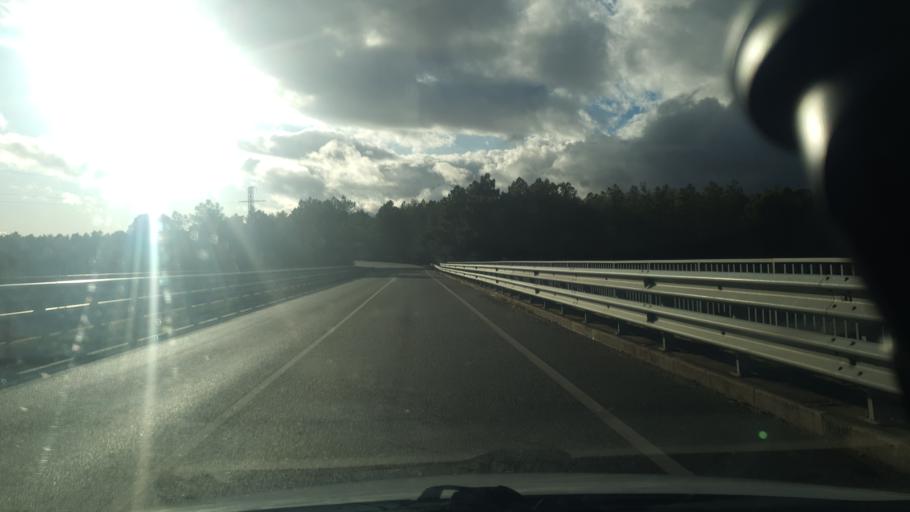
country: ES
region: Castille and Leon
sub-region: Provincia de Segovia
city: Santiuste de San Juan Bautista
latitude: 41.1520
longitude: -4.5363
